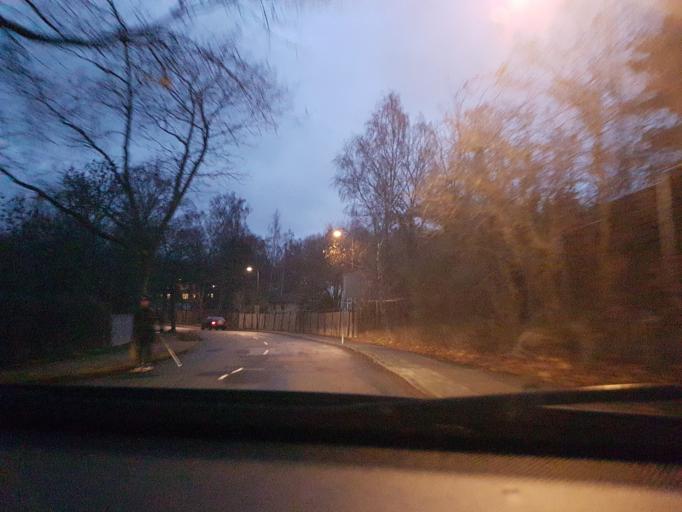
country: DK
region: Capital Region
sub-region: Gentofte Kommune
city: Charlottenlund
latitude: 55.7734
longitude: 12.5798
